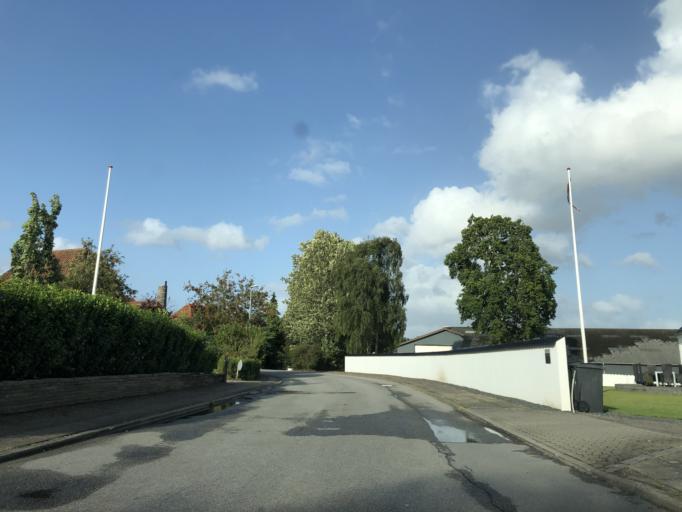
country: DK
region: South Denmark
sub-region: Haderslev Kommune
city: Starup
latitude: 55.1926
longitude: 9.5202
